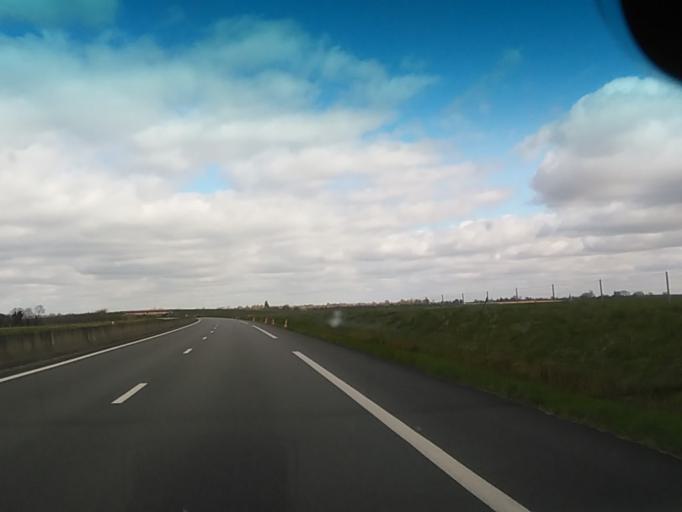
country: FR
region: Haute-Normandie
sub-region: Departement de l'Eure
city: Thiberville
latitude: 49.1160
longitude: 0.5243
